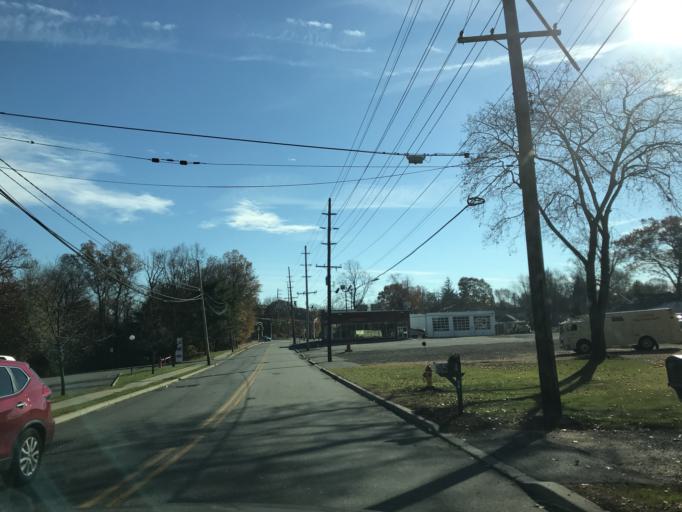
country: US
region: New Jersey
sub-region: Morris County
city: Boonton
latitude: 40.8942
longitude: -74.4167
